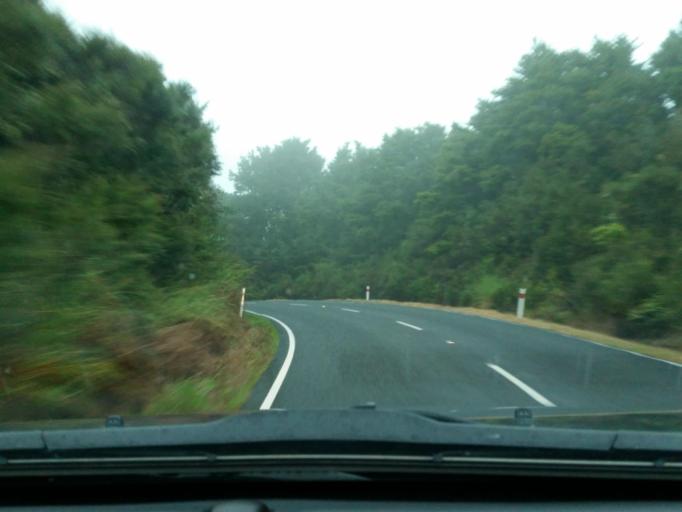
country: NZ
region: Northland
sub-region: Kaipara District
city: Dargaville
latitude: -35.8410
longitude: 174.0306
